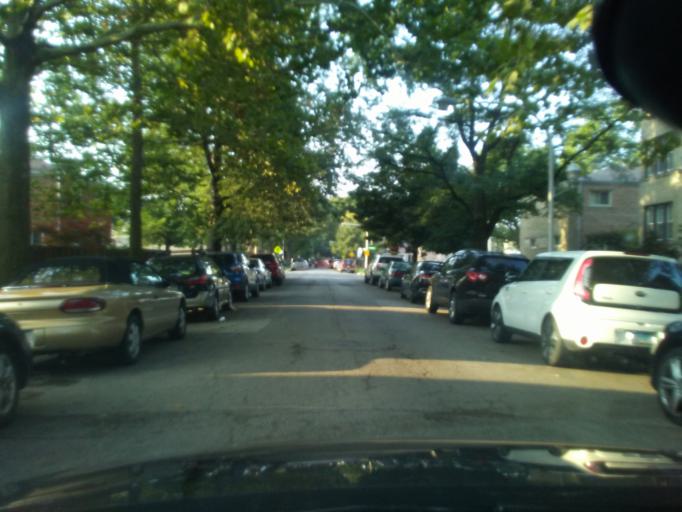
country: US
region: Illinois
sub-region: Cook County
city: Evanston
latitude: 42.0162
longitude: -87.6889
